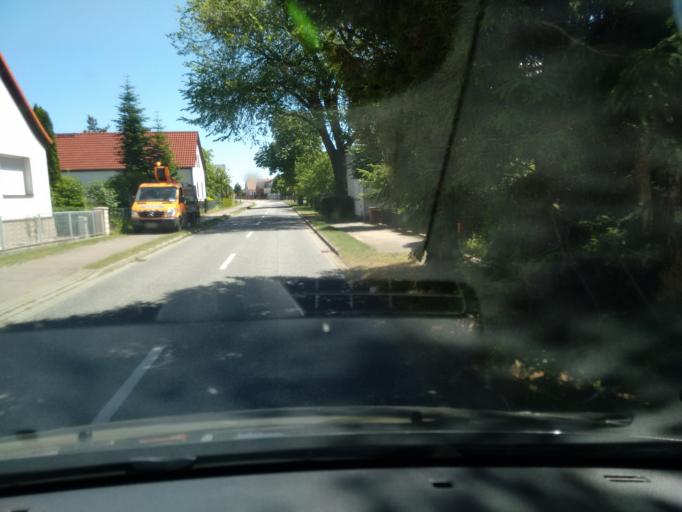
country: DE
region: Brandenburg
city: Beeskow
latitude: 52.1950
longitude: 14.3047
